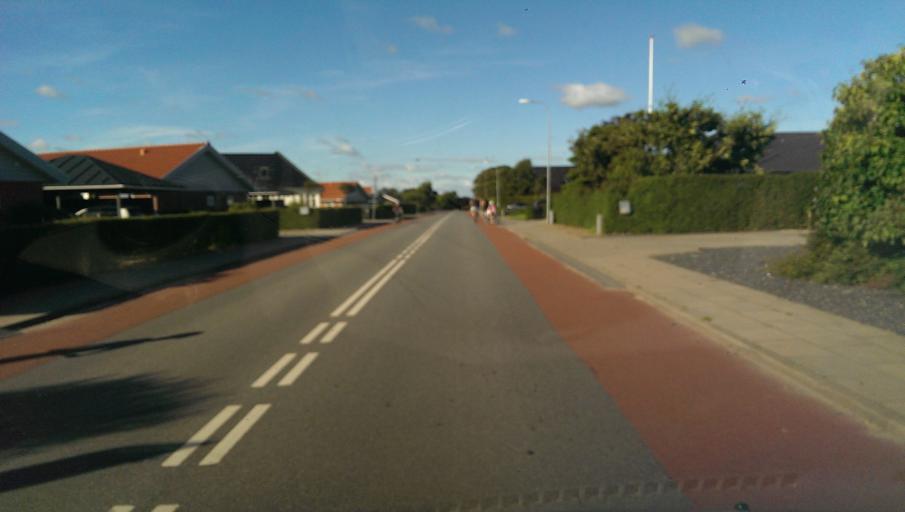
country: DK
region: South Denmark
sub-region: Esbjerg Kommune
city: Esbjerg
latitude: 55.5331
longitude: 8.4740
